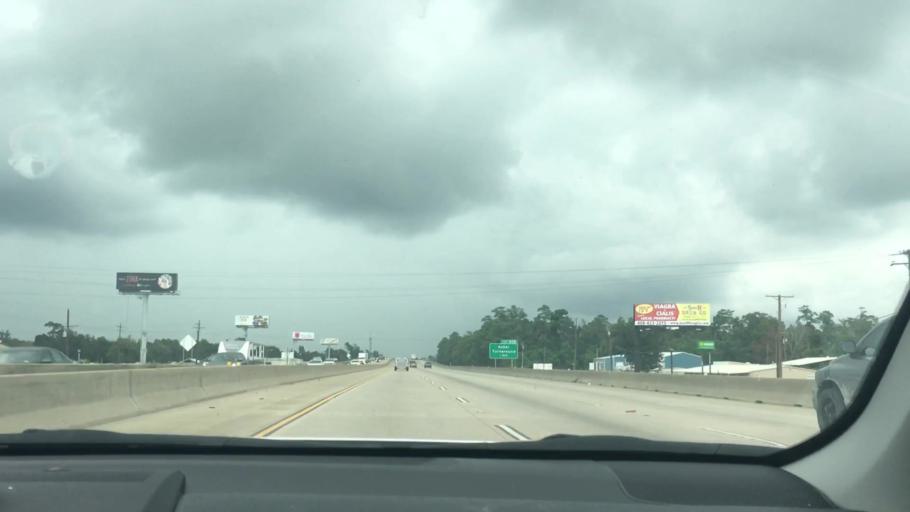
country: US
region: Texas
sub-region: Jefferson County
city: Beaumont
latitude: 30.0988
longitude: -94.0656
